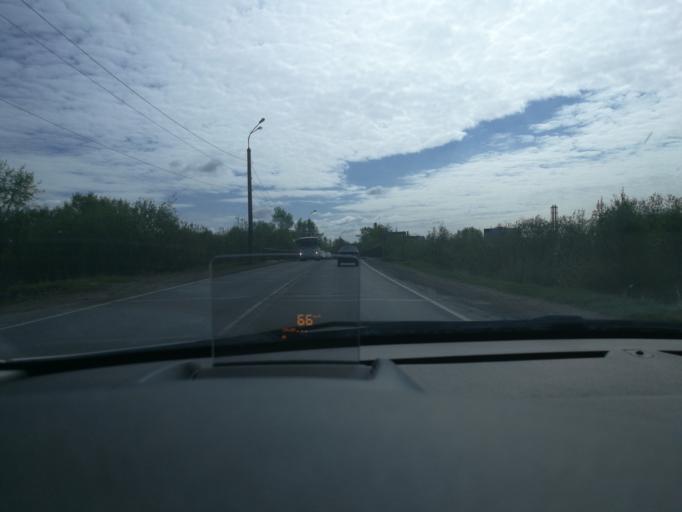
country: RU
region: Arkhangelskaya
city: Arkhangel'sk
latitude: 64.5972
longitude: 40.5407
